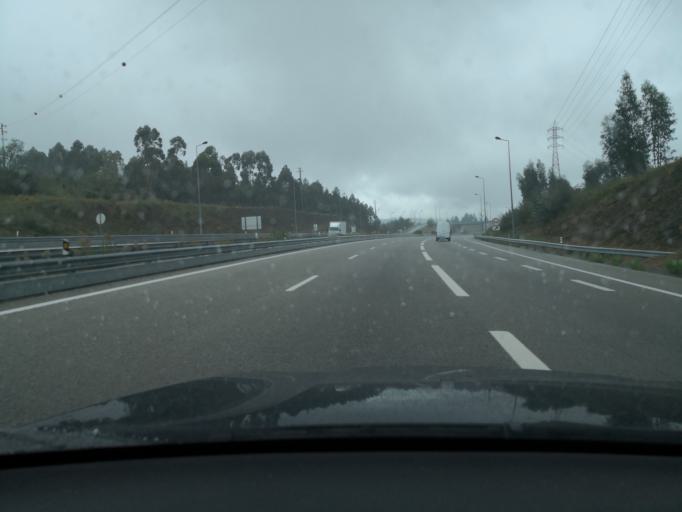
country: PT
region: Porto
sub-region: Pacos de Ferreira
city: Seroa
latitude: 41.2480
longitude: -8.4347
